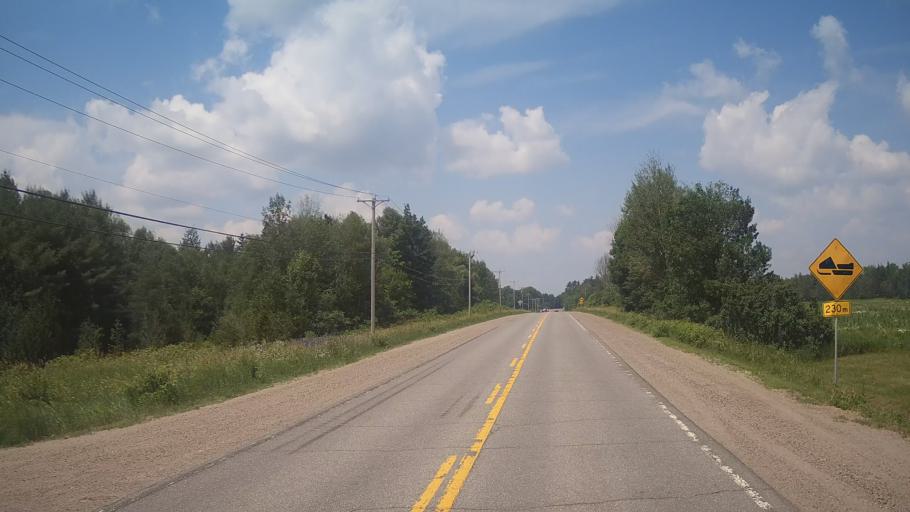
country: CA
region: Quebec
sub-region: Outaouais
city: Shawville
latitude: 45.5711
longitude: -76.4374
